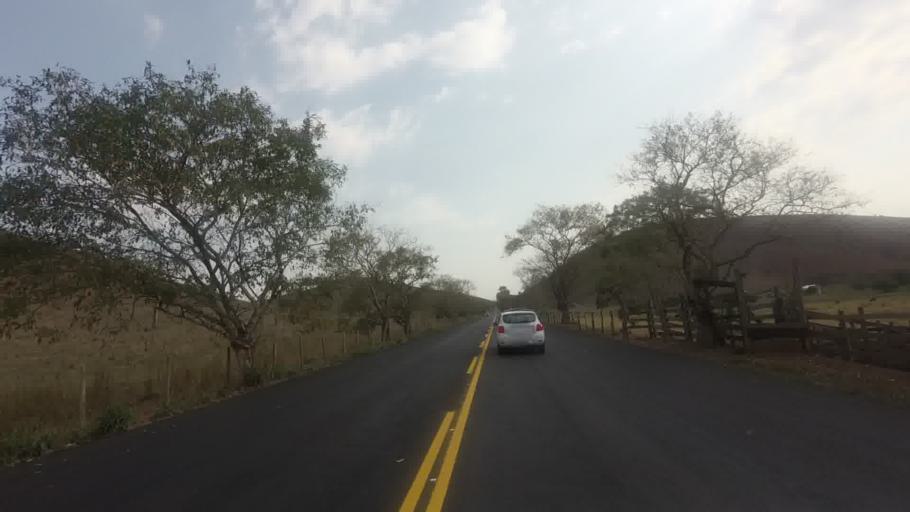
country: BR
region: Rio de Janeiro
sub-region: Bom Jesus Do Itabapoana
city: Bom Jesus do Itabapoana
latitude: -21.2285
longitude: -41.7451
